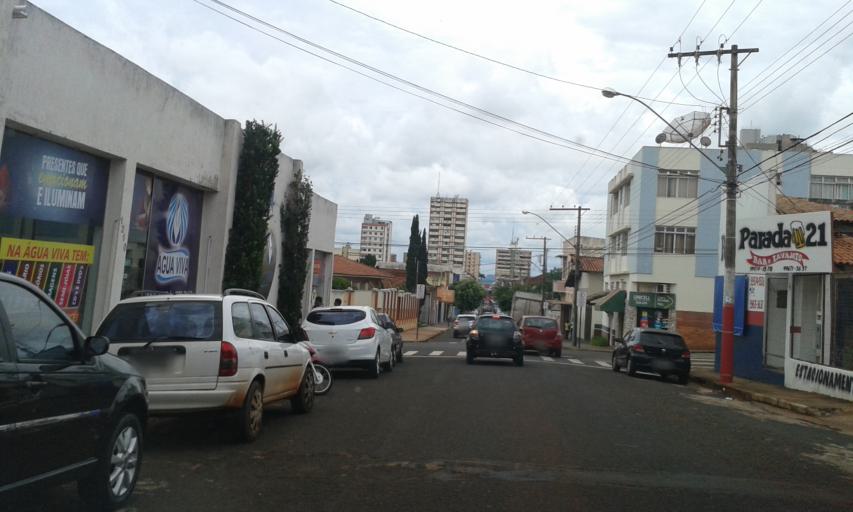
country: BR
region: Minas Gerais
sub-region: Ituiutaba
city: Ituiutaba
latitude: -18.9779
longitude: -49.4614
